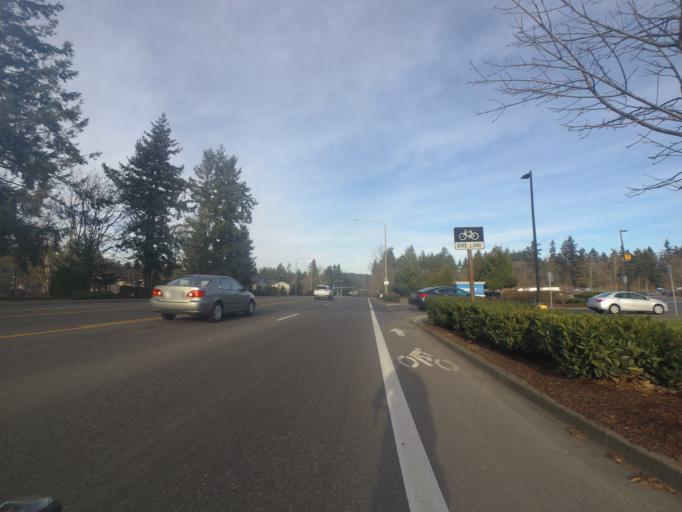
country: US
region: Washington
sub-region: Pierce County
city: Lakewood
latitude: 47.1931
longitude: -122.5193
